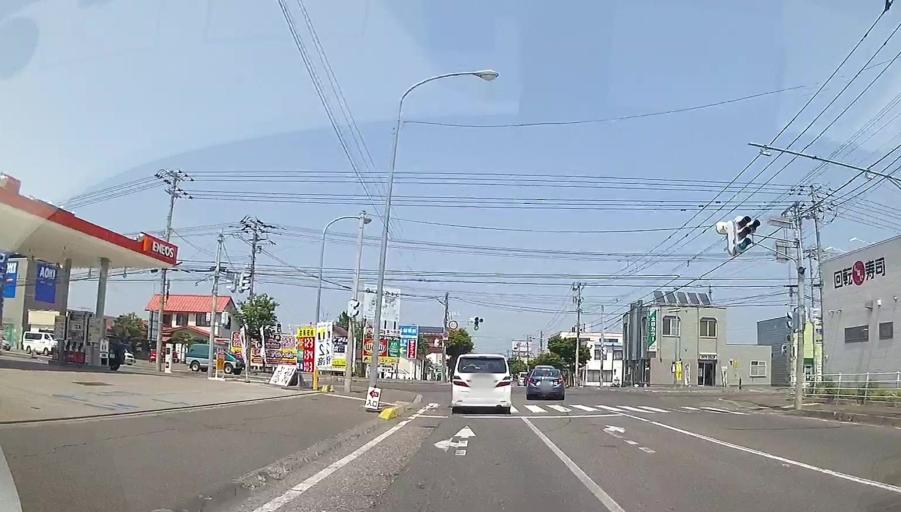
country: JP
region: Hokkaido
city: Obihiro
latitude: 42.8915
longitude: 143.2014
